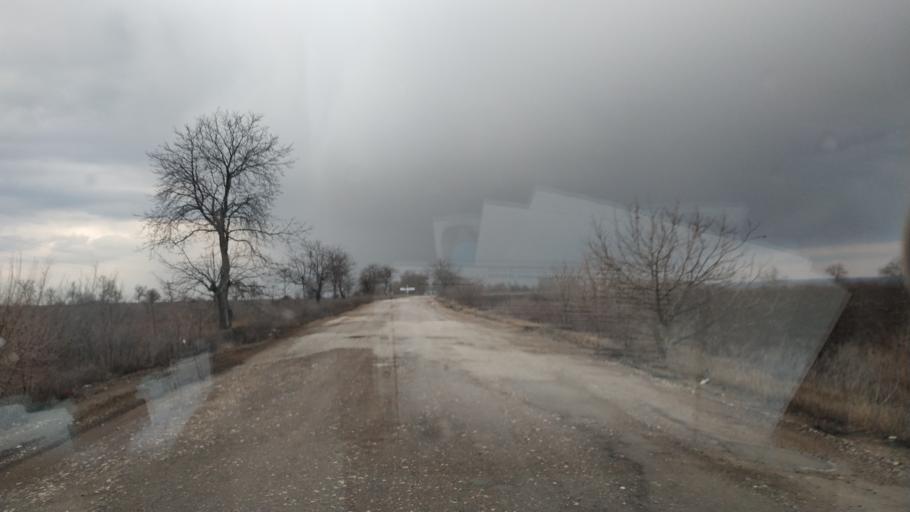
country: MD
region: Telenesti
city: Grigoriopol
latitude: 47.0664
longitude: 29.2999
